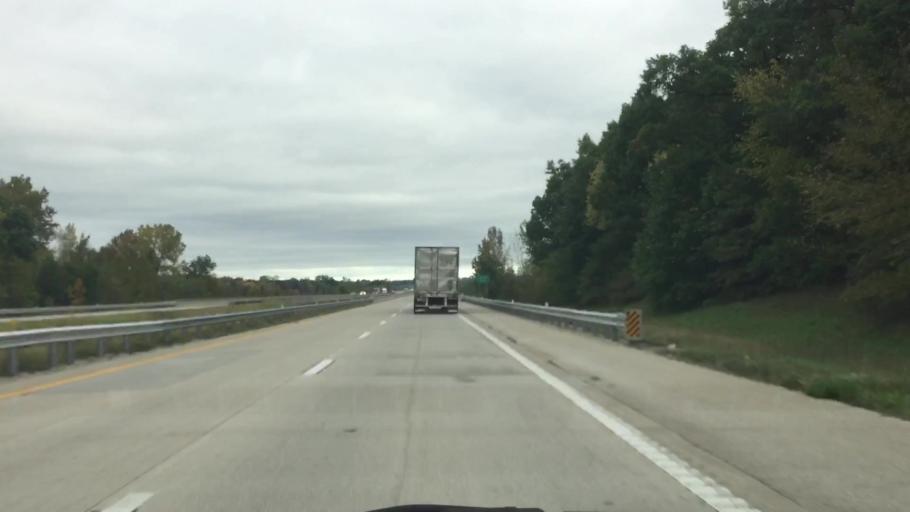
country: US
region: Missouri
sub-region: Daviess County
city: Gallatin
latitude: 40.0210
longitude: -94.0957
